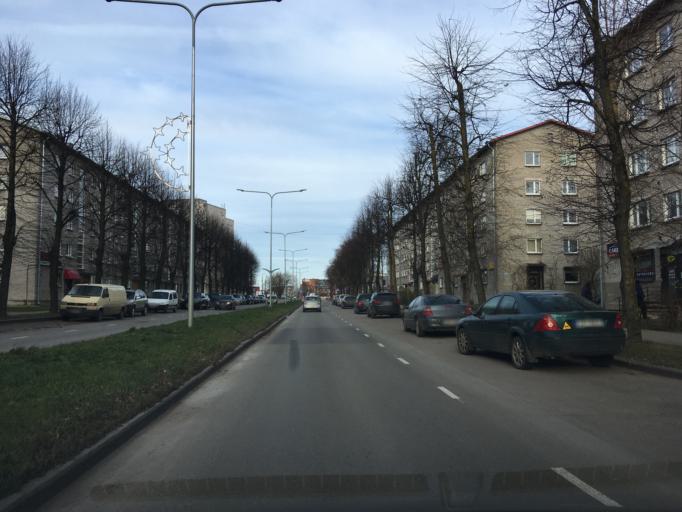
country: EE
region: Ida-Virumaa
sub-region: Narva linn
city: Narva
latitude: 59.3771
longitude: 28.1806
